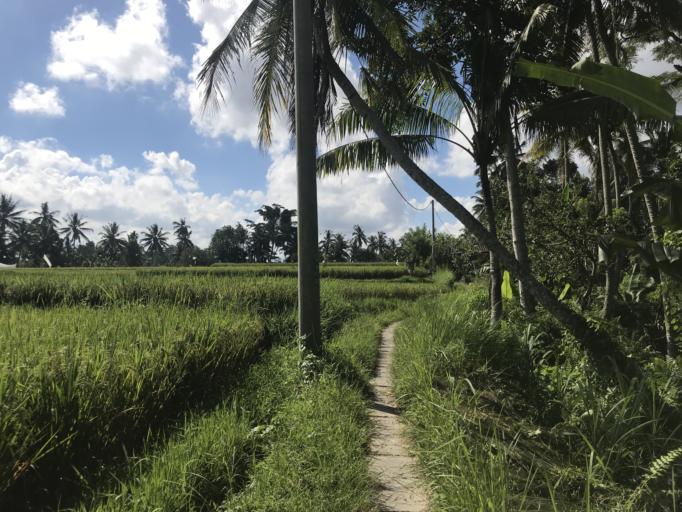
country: ID
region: Bali
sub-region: Kabupaten Gianyar
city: Ubud
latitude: -8.4887
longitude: 115.2616
